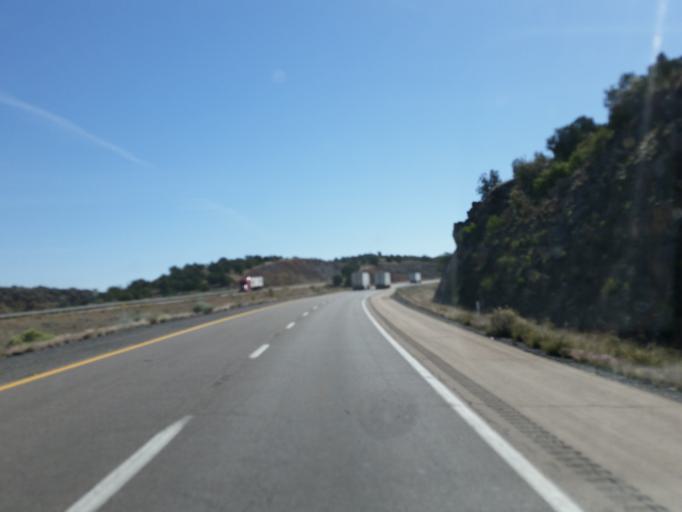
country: US
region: Arizona
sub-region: Mohave County
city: Peach Springs
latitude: 35.1883
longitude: -113.4449
